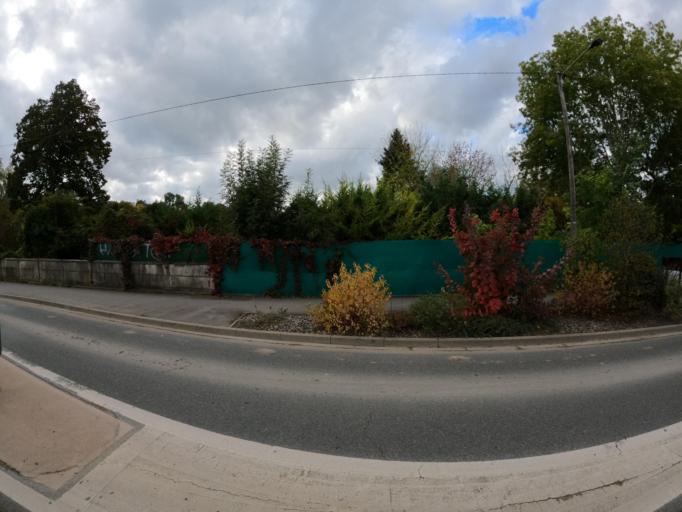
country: FR
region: Ile-de-France
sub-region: Departement de Seine-et-Marne
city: Esbly
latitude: 48.9104
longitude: 2.8151
